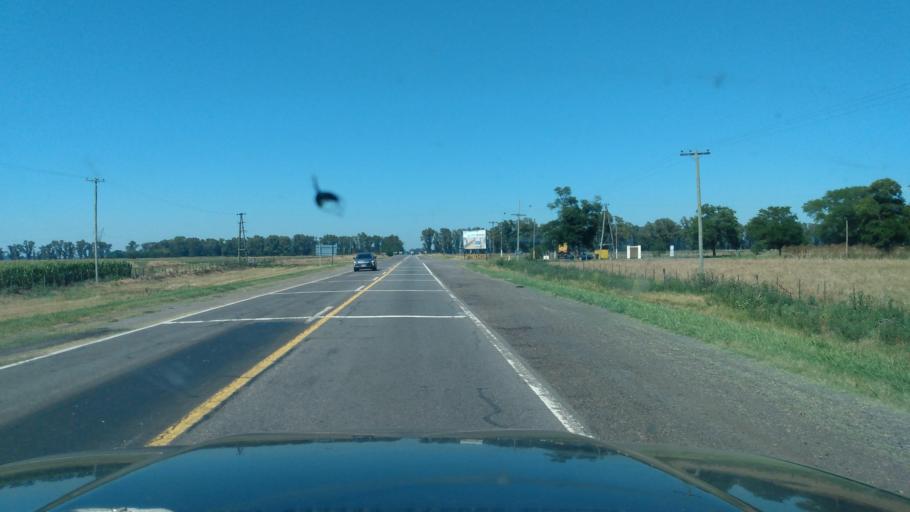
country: AR
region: Buenos Aires
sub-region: Partido de Bragado
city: Bragado
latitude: -35.0907
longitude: -60.3927
